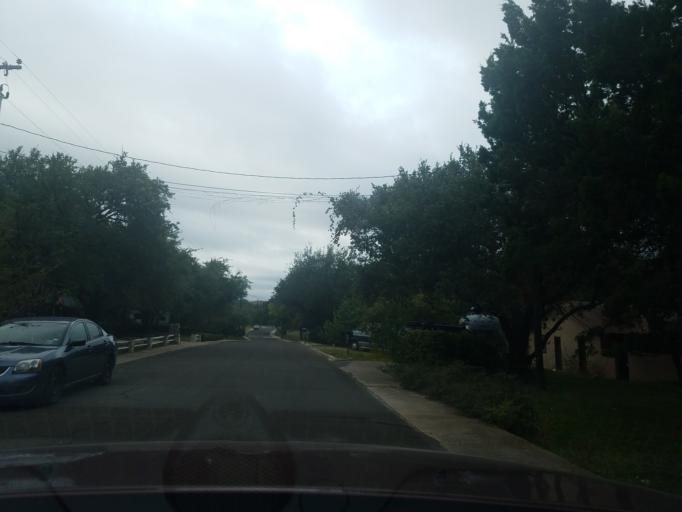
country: US
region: Texas
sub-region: Williamson County
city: Anderson Mill
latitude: 30.4798
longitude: -97.8120
